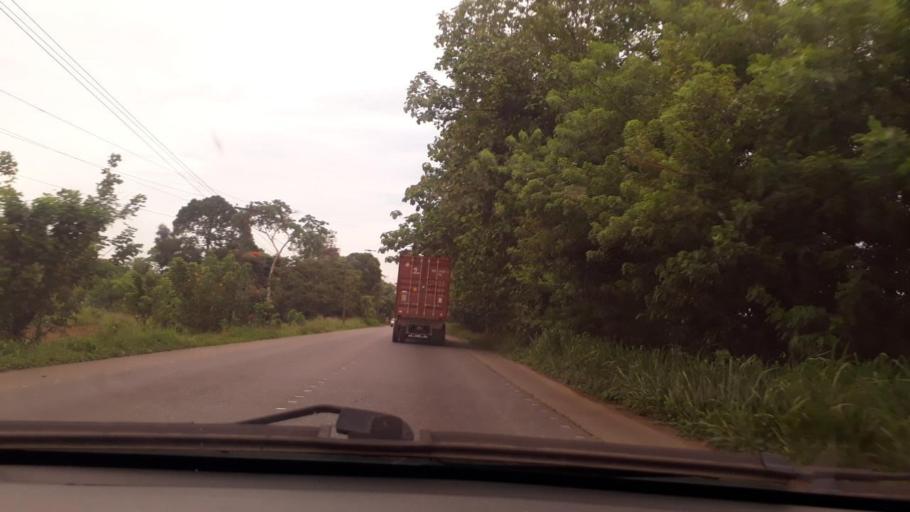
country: GT
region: Izabal
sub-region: Municipio de Puerto Barrios
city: Puerto Barrios
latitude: 15.5877
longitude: -88.5787
